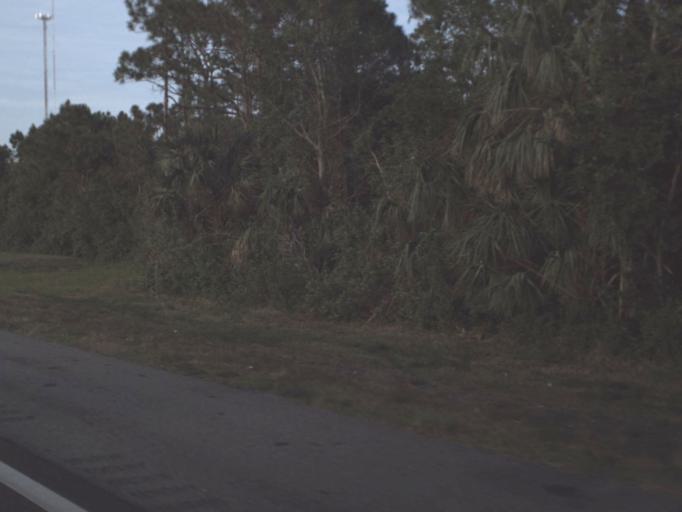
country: US
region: Florida
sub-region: Brevard County
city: Titusville
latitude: 28.5771
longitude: -80.8513
